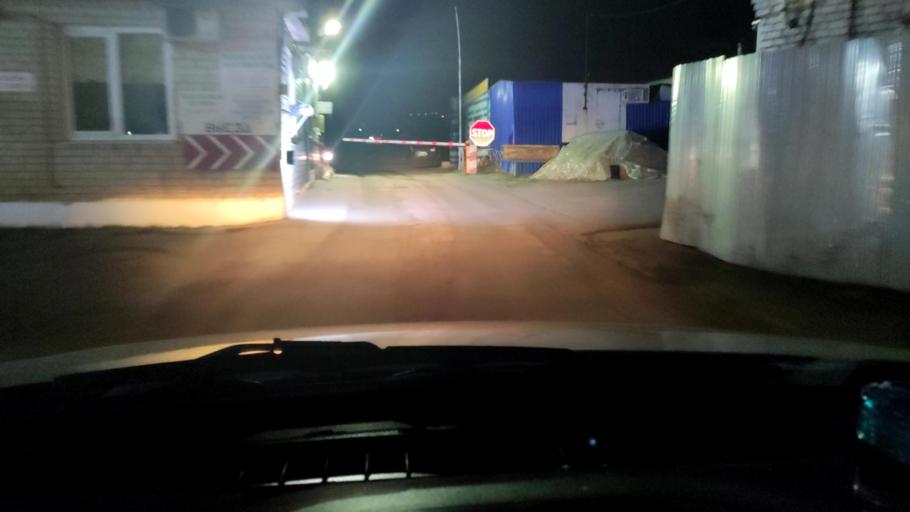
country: RU
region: Voronezj
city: Voronezh
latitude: 51.6383
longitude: 39.1300
